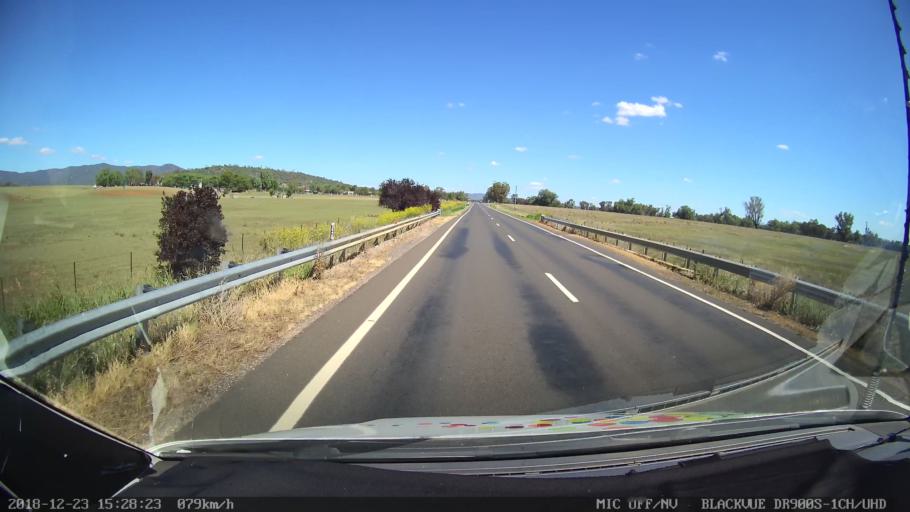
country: AU
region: New South Wales
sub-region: Tamworth Municipality
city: East Tamworth
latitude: -30.9357
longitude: 150.8519
